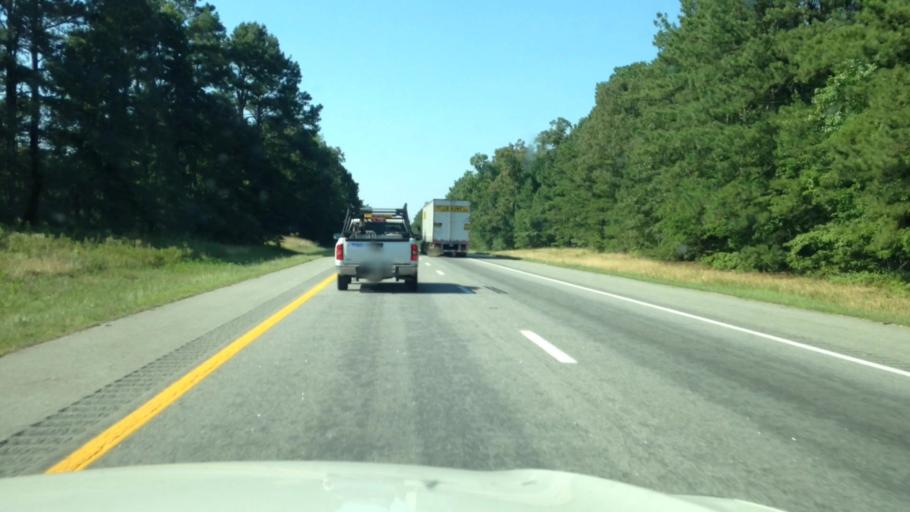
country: US
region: Virginia
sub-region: City of Emporia
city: Emporia
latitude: 36.7801
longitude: -77.4619
